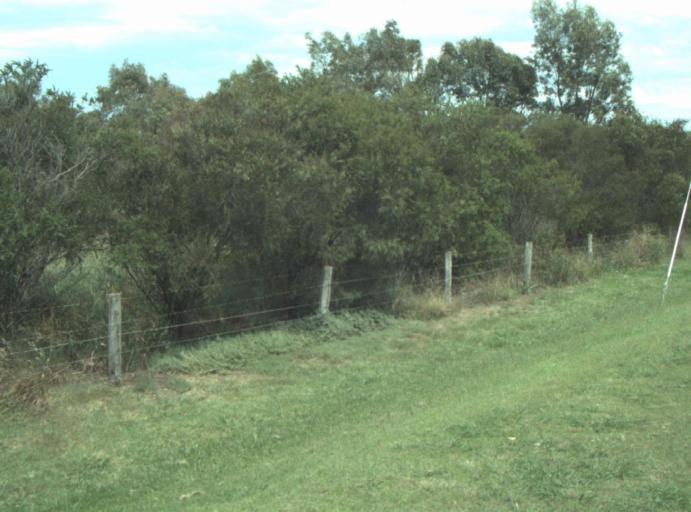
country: AU
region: Victoria
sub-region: Greater Geelong
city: Clifton Springs
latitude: -38.1351
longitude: 144.6252
